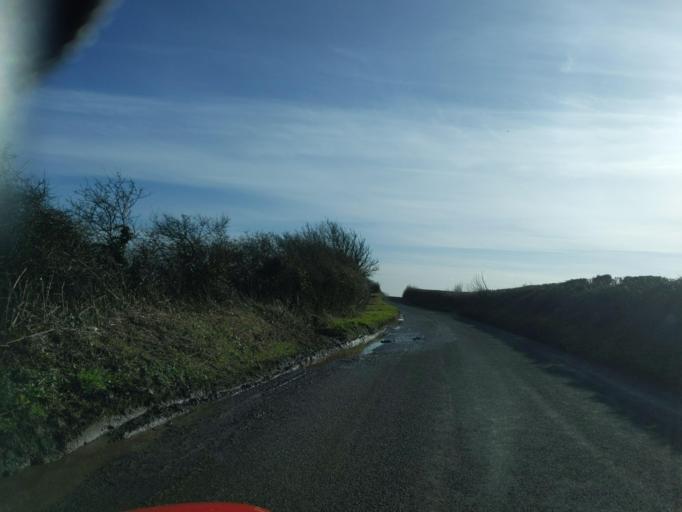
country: GB
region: England
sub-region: Devon
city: Kingsbridge
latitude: 50.3479
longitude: -3.7277
